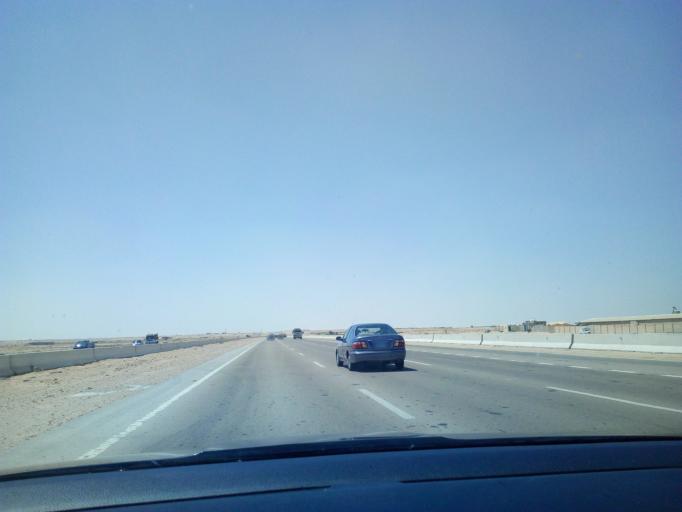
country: EG
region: Al Buhayrah
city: Abu al Matamir
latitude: 30.5736
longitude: 29.9314
